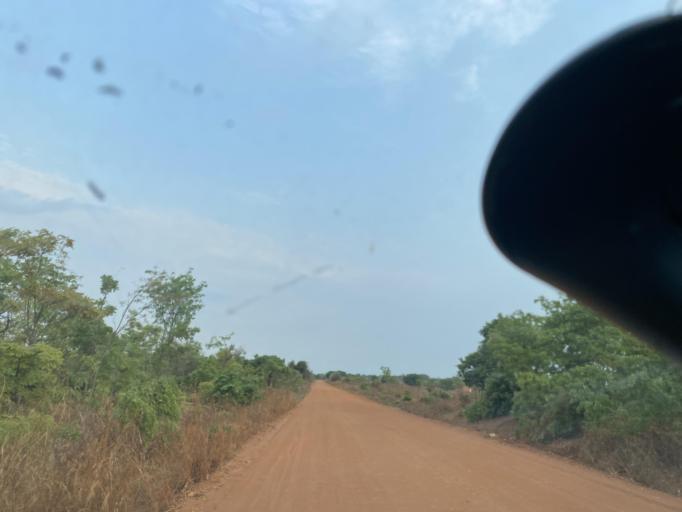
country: ZM
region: Lusaka
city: Chongwe
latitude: -15.2374
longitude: 28.5947
